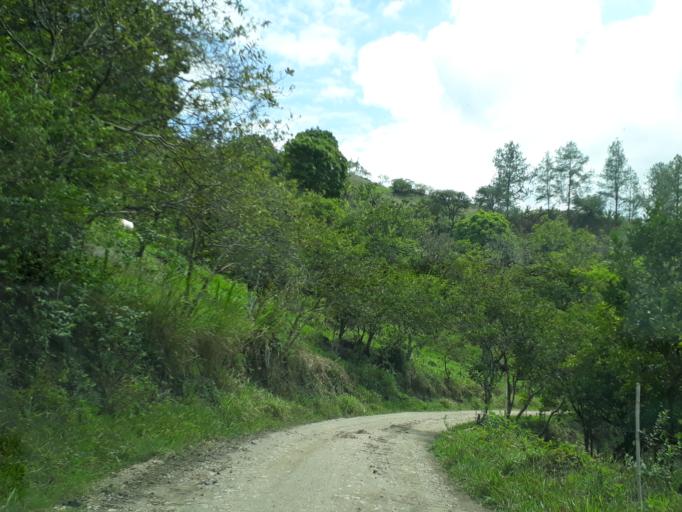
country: CO
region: Cundinamarca
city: Manta
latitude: 5.0043
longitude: -73.5207
